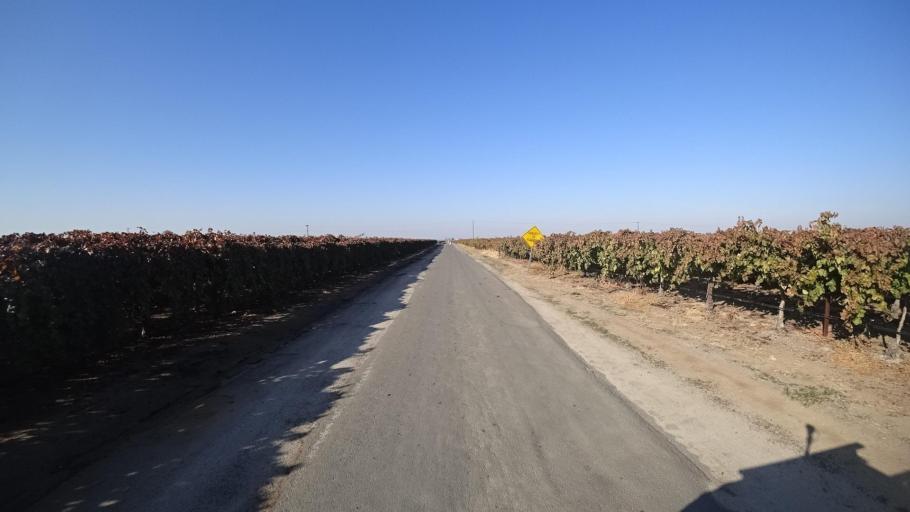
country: US
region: California
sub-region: Kern County
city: McFarland
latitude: 35.7253
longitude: -119.1673
